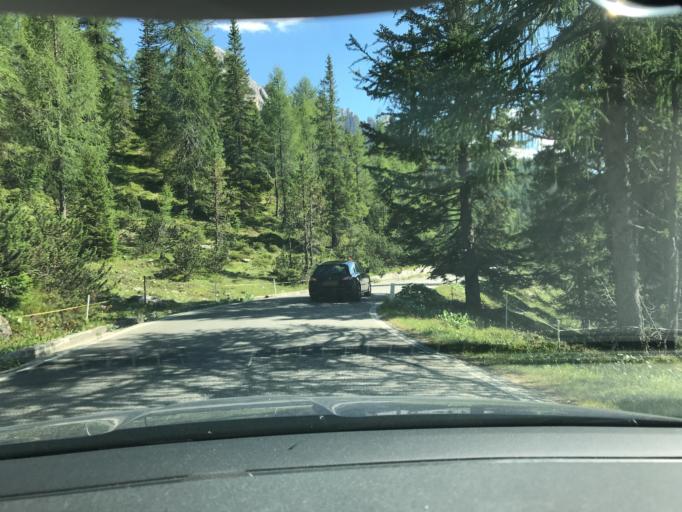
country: IT
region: Trentino-Alto Adige
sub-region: Bolzano
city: Sesto
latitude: 46.6054
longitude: 12.2754
